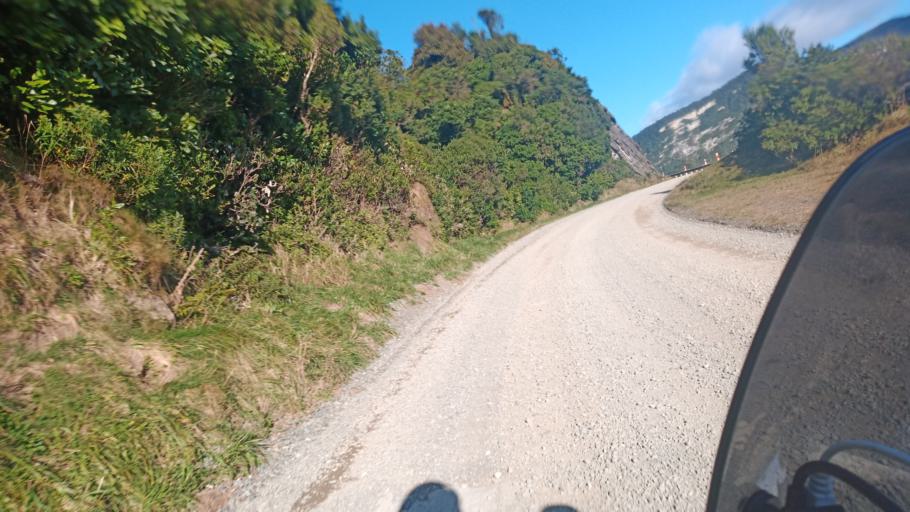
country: NZ
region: Hawke's Bay
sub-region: Wairoa District
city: Wairoa
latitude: -38.7878
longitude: 177.1302
